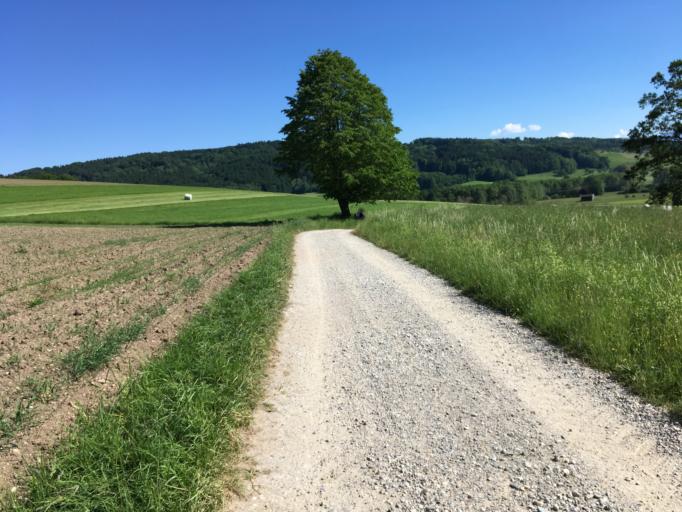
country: DE
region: Bavaria
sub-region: Upper Bavaria
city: Bad Endorf
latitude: 47.8958
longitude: 12.2927
